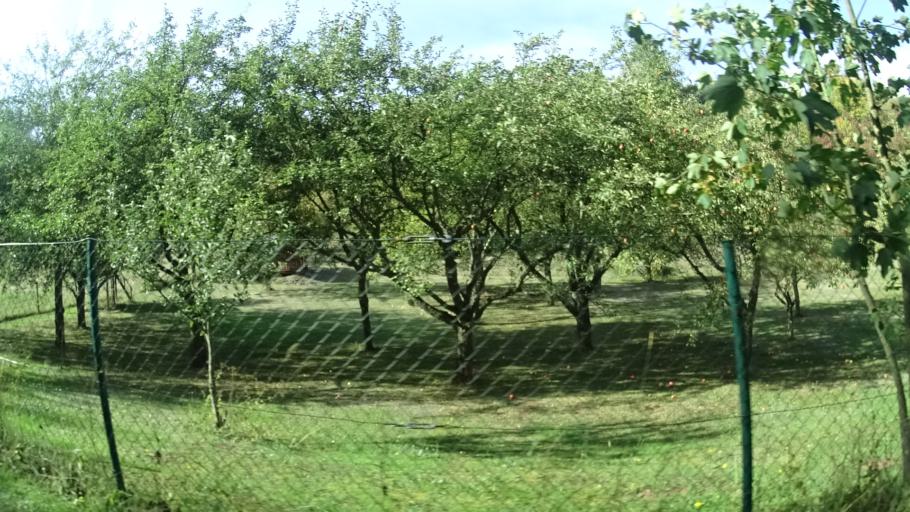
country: DE
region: Thuringia
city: Stepfershausen
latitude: 50.5905
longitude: 10.2977
